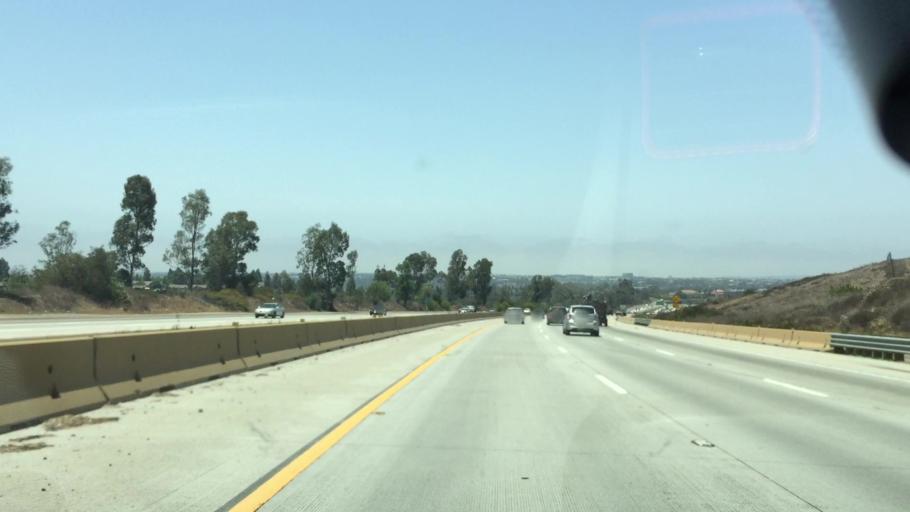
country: US
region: California
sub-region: San Diego County
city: La Mesa
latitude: 32.8446
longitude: -117.0819
